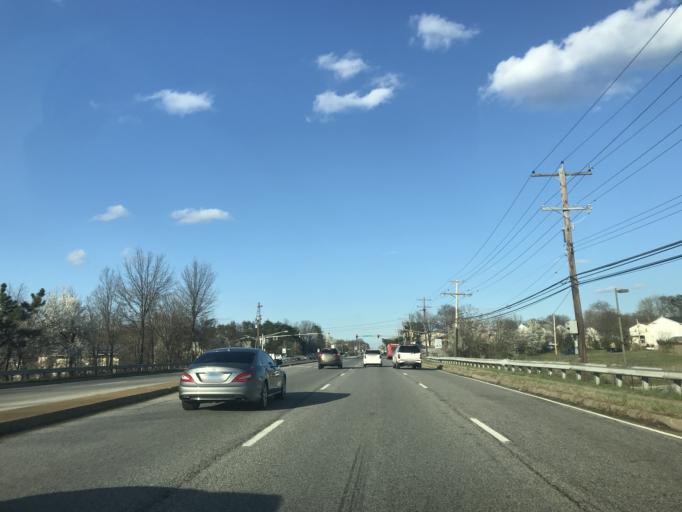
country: US
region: Maryland
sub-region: Prince George's County
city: Glenarden
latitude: 38.9330
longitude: -76.8661
